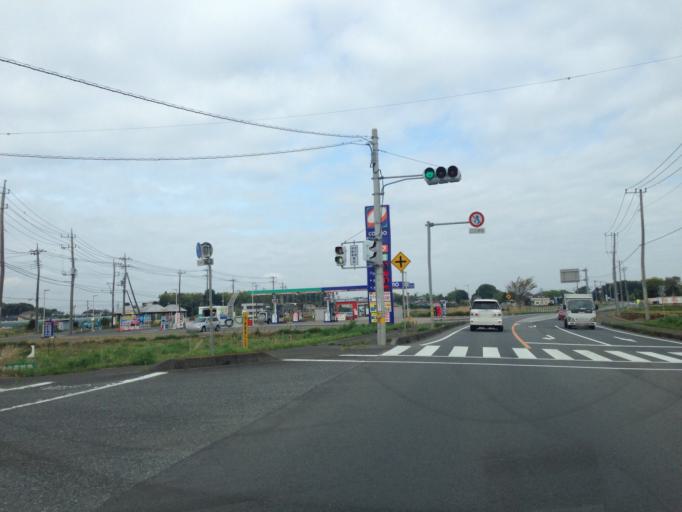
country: JP
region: Ibaraki
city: Ishige
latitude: 36.1440
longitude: 140.0304
